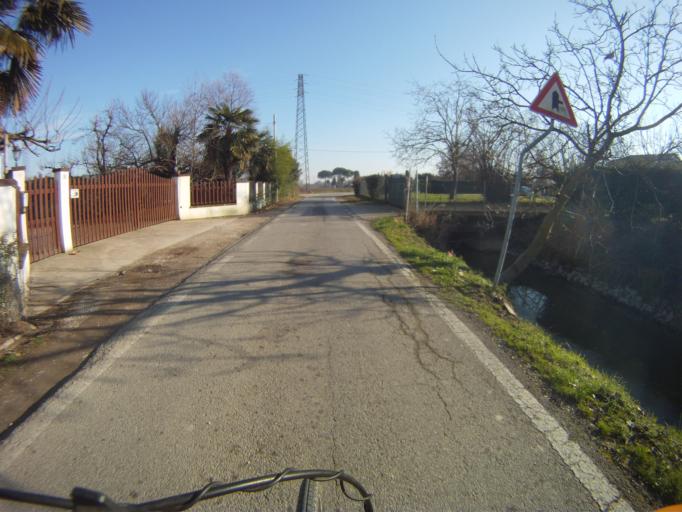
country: IT
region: Veneto
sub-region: Provincia di Padova
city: Piove di Sacco-Piovega
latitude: 45.2934
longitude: 12.0162
